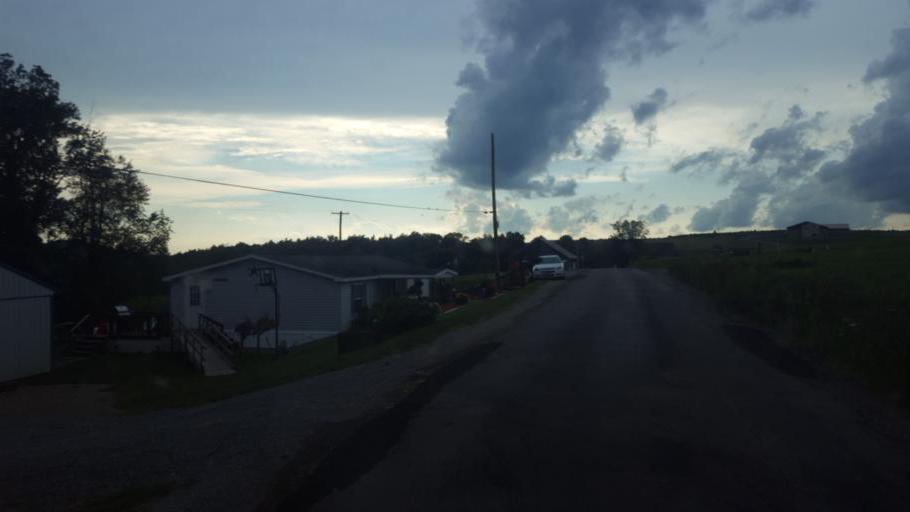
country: US
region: Pennsylvania
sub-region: Clarion County
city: Clarion
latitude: 41.1784
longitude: -79.3914
